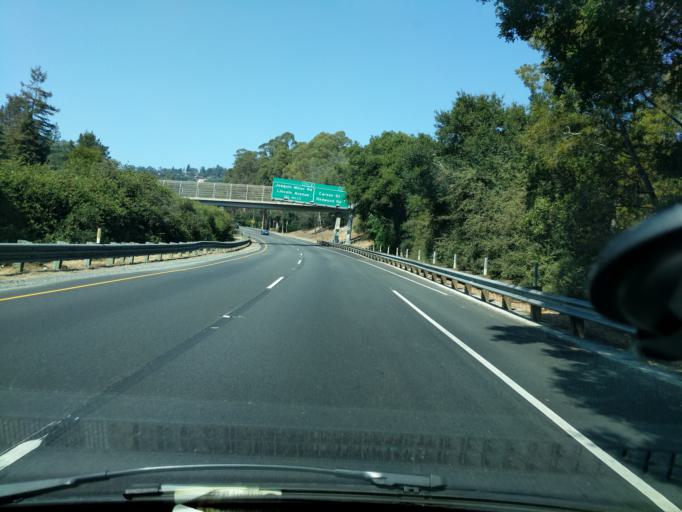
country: US
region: California
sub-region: Alameda County
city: Piedmont
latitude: 37.7909
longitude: -122.1809
